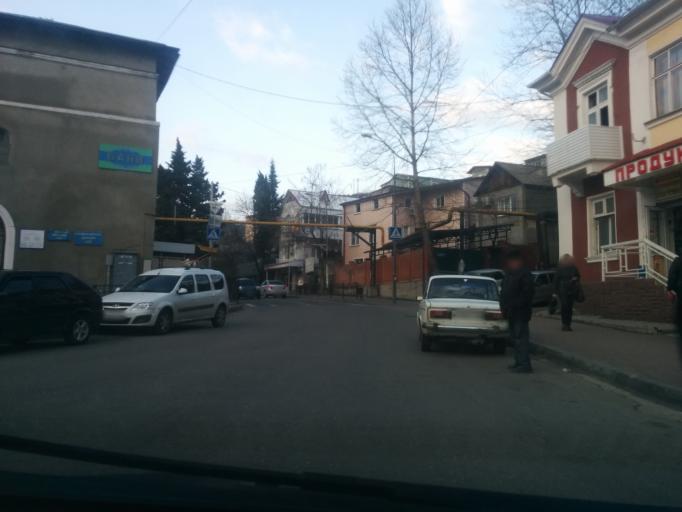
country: RU
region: Krasnodarskiy
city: Tuapse
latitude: 44.1006
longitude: 39.0726
